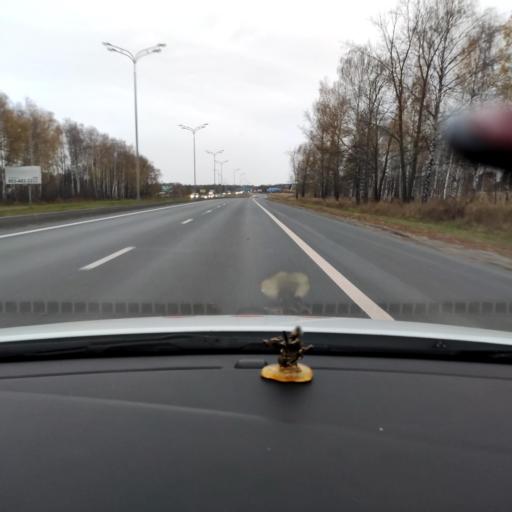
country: RU
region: Tatarstan
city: Osinovo
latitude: 55.8641
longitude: 48.7960
